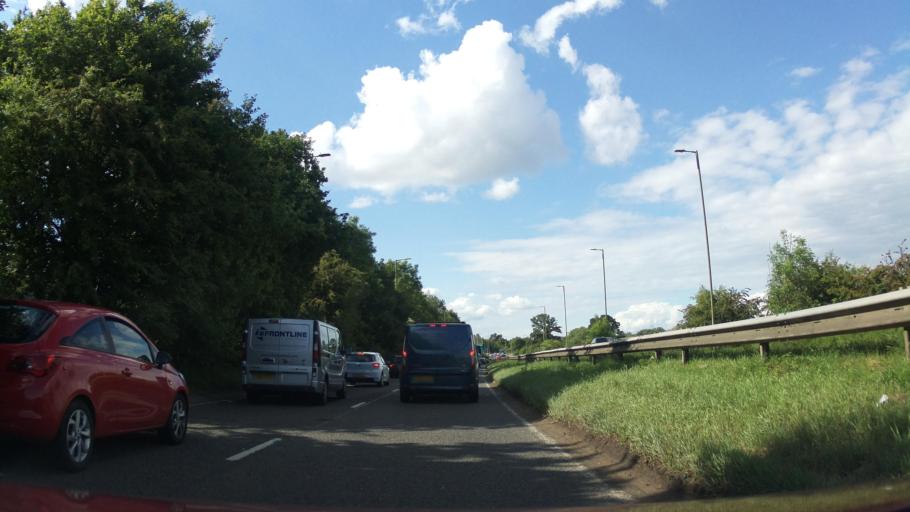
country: GB
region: England
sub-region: Hertfordshire
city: Kings Langley
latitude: 51.6960
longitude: -0.4397
